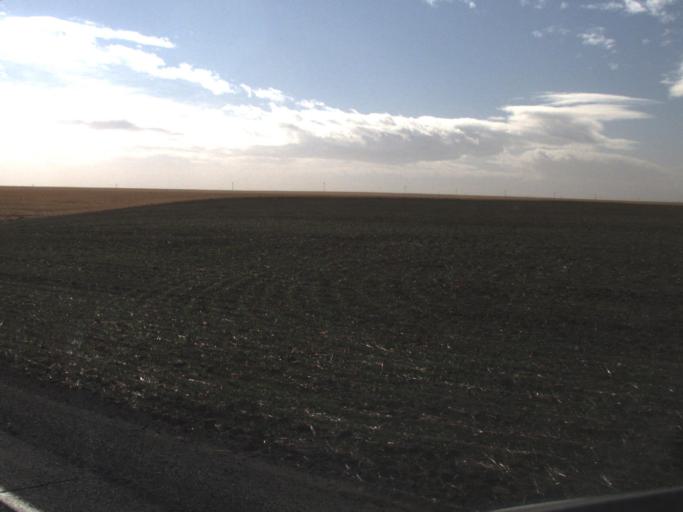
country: US
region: Washington
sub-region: Okanogan County
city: Coulee Dam
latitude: 47.6499
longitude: -118.7211
